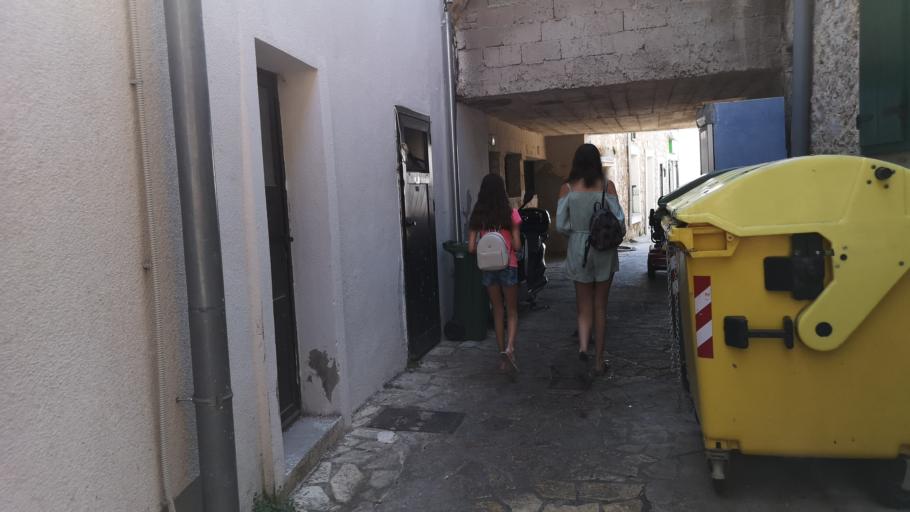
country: HR
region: Sibensko-Kniniska
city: Vodice
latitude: 43.7568
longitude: 15.7745
